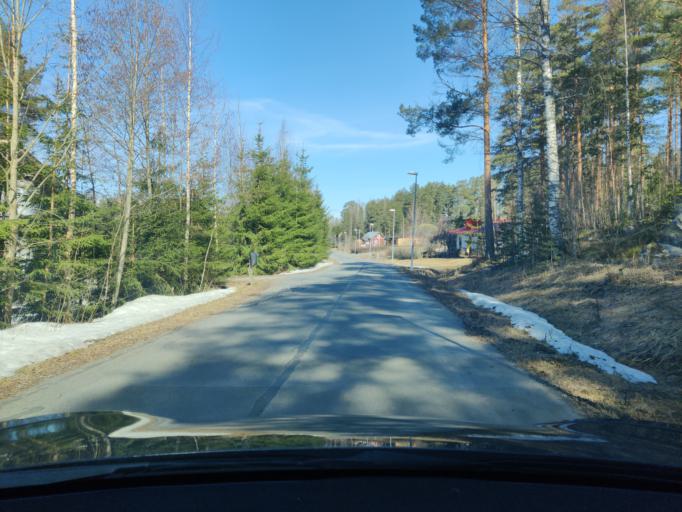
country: FI
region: Northern Savo
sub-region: Kuopio
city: Vehmersalmi
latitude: 62.7574
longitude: 28.0327
